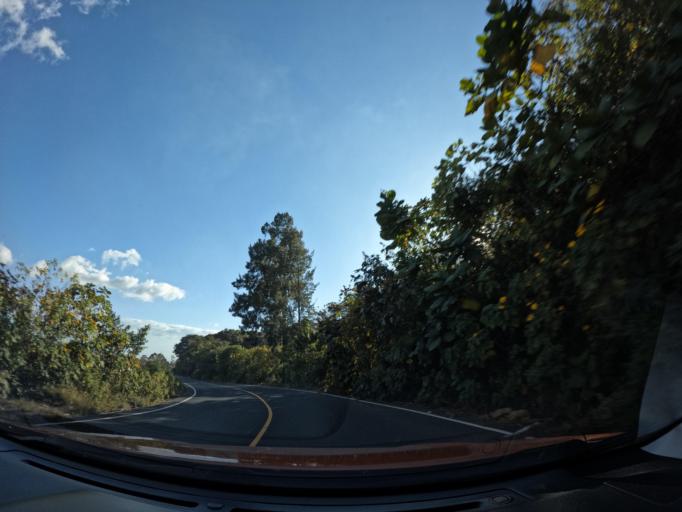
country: GT
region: Escuintla
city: Palin
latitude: 14.4644
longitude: -90.6939
